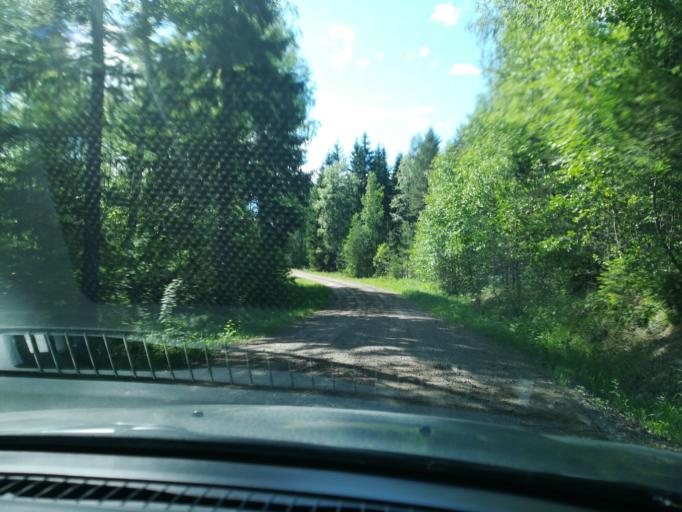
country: FI
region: Southern Savonia
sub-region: Mikkeli
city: Puumala
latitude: 61.6520
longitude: 28.1767
